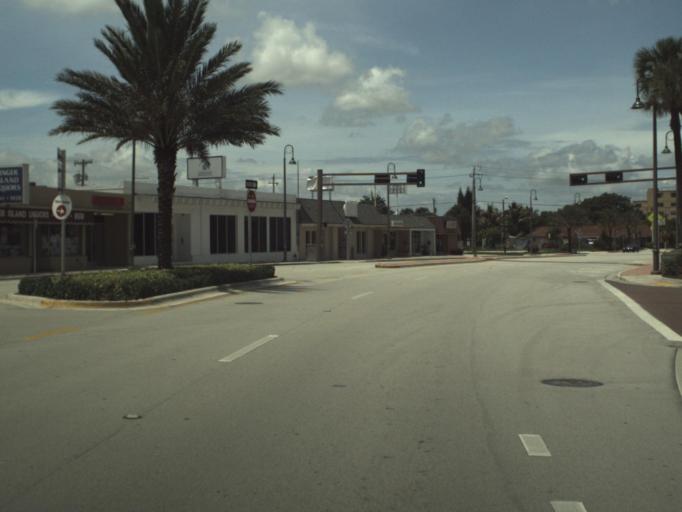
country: US
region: Florida
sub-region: Palm Beach County
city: Palm Beach Shores
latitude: 26.7840
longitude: -80.0359
